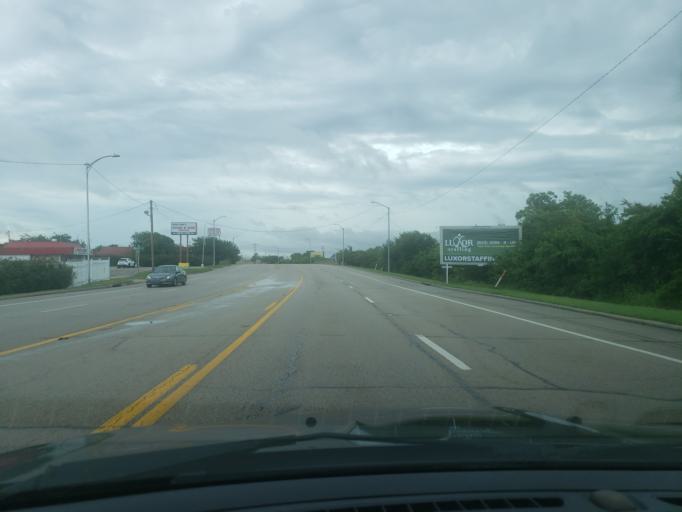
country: US
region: Texas
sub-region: Dallas County
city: Grand Prairie
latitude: 32.7420
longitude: -97.0173
